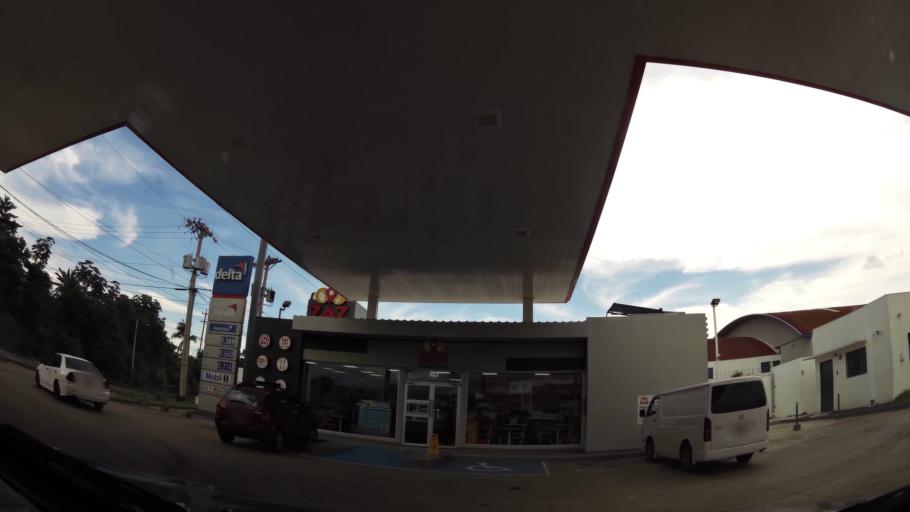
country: PA
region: Panama
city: Tocumen
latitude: 9.0909
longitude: -79.3958
